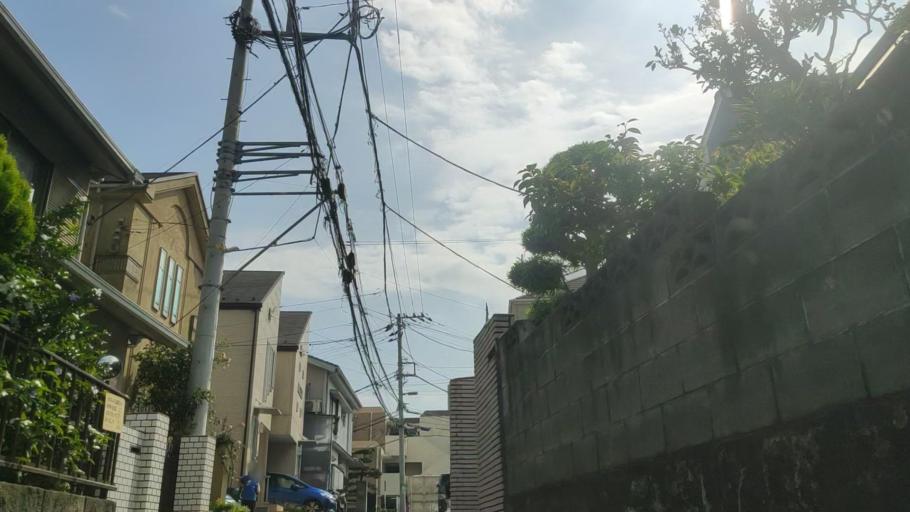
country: JP
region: Kanagawa
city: Yokohama
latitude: 35.4232
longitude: 139.6150
